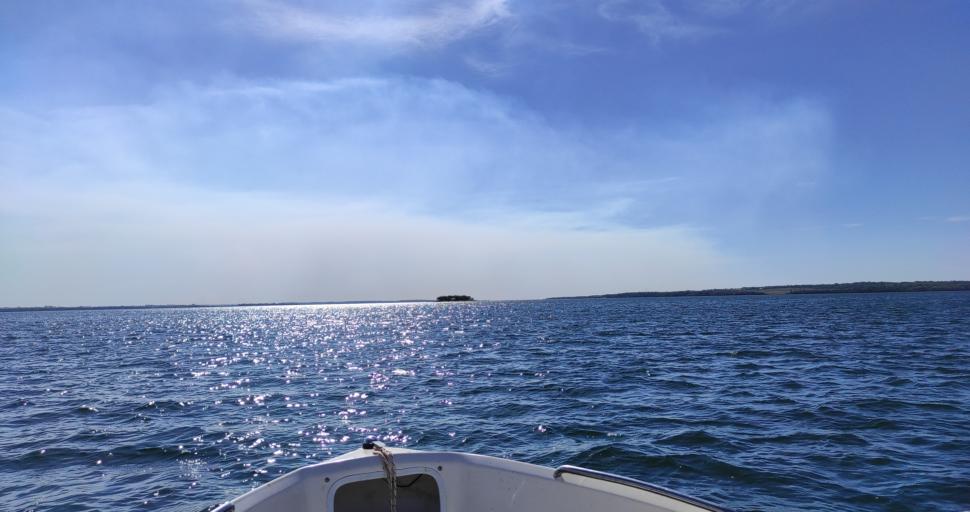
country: AR
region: Misiones
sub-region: Departamento de Capital
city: Posadas
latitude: -27.3434
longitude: -55.9350
